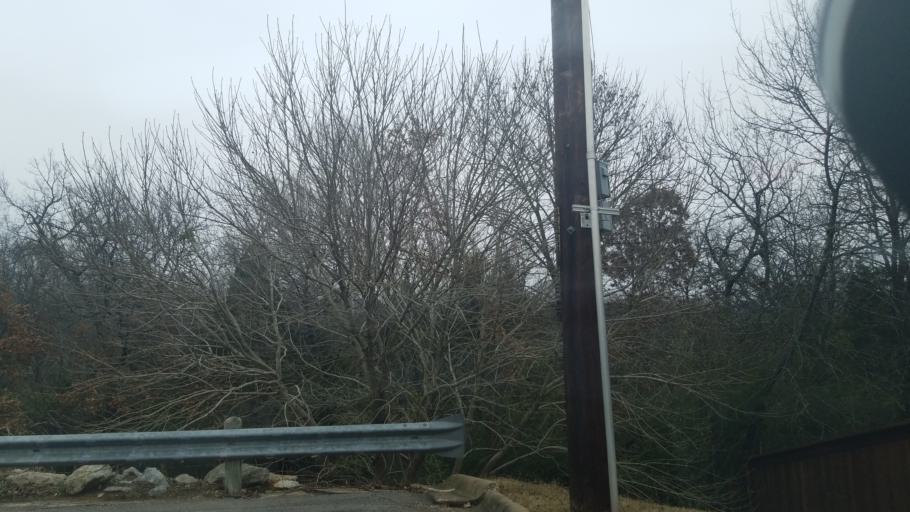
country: US
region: Texas
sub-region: Denton County
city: Corinth
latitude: 33.1542
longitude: -97.1238
